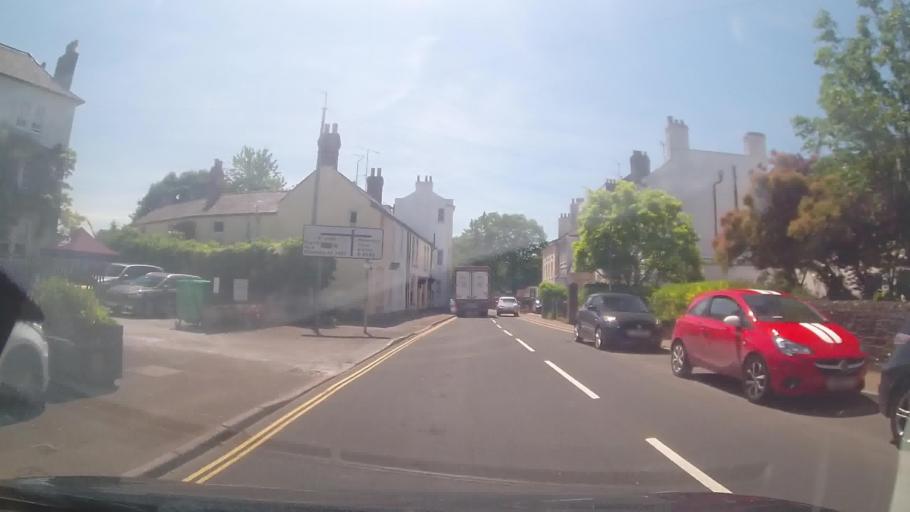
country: GB
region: Wales
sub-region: Monmouthshire
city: Monmouth
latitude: 51.8155
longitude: -2.7126
